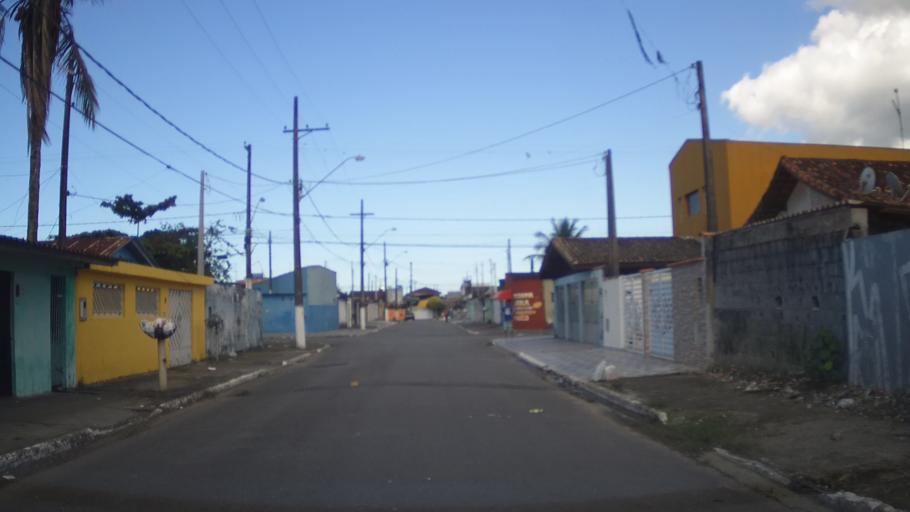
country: BR
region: Sao Paulo
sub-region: Praia Grande
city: Praia Grande
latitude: -24.0280
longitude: -46.5081
